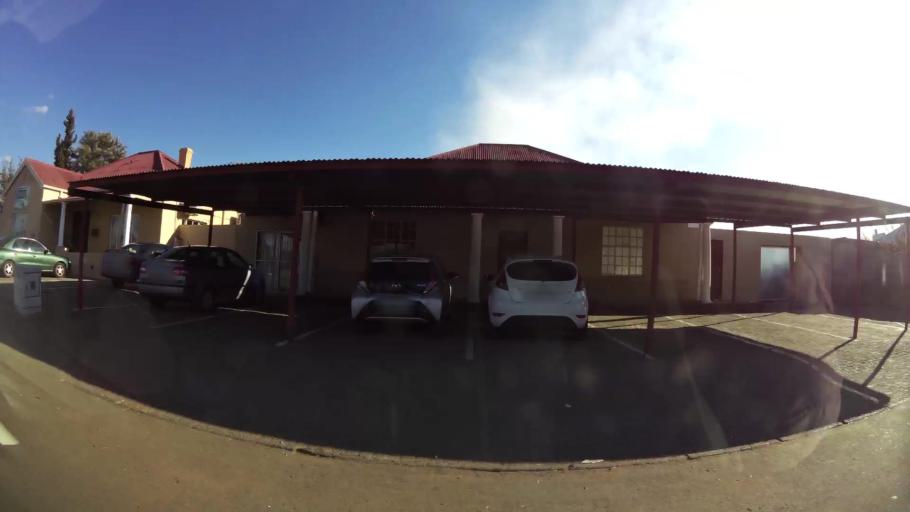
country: ZA
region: Northern Cape
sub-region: Frances Baard District Municipality
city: Kimberley
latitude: -28.7468
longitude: 24.7590
